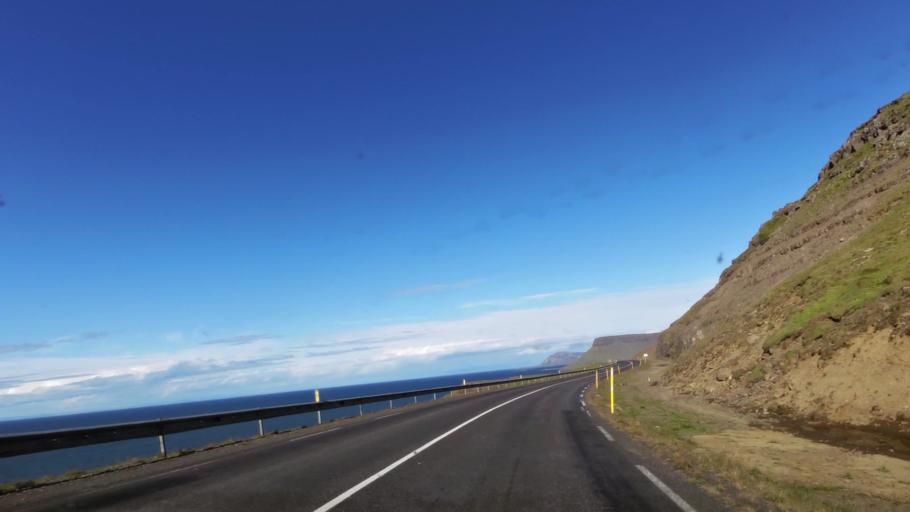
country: IS
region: West
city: Olafsvik
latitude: 64.9484
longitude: -23.4861
